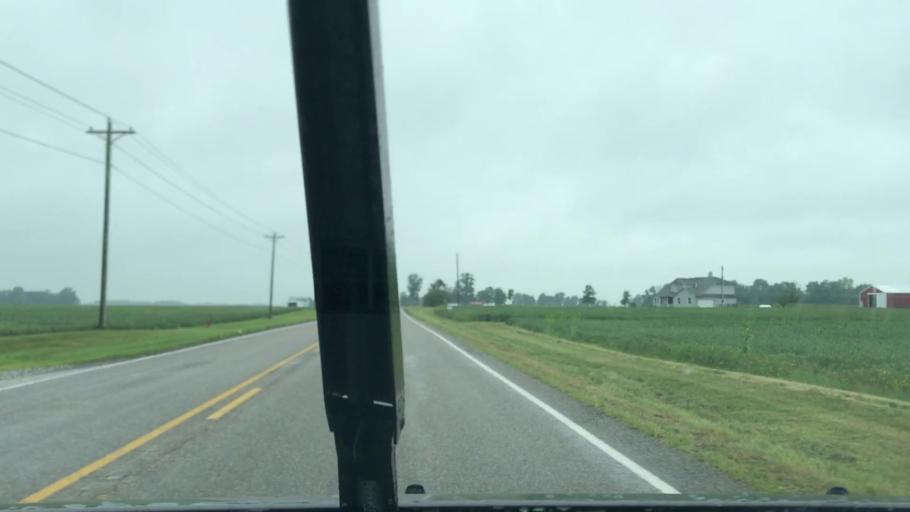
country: US
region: Indiana
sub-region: Boone County
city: Lebanon
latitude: 40.1264
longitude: -86.4435
